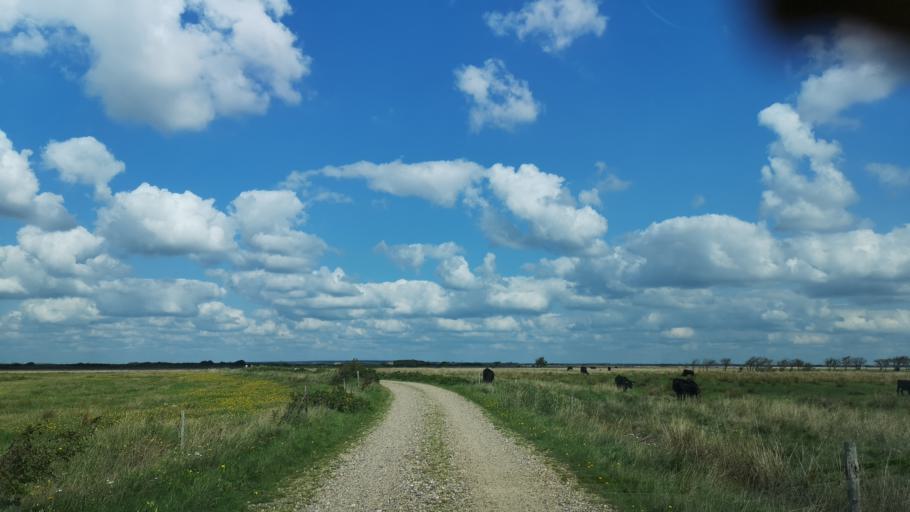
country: DK
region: Central Jutland
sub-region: Ringkobing-Skjern Kommune
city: Skjern
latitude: 55.9072
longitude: 8.3996
